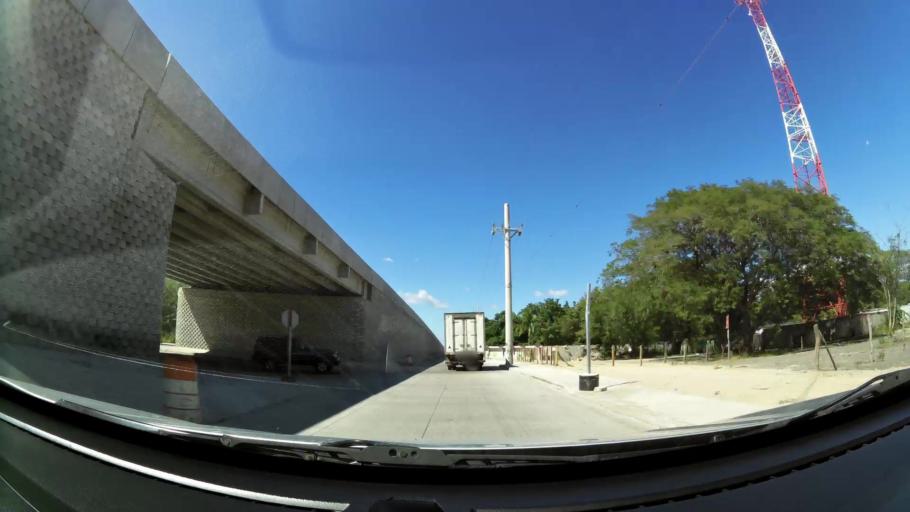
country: CR
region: Guanacaste
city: Liberia
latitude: 10.6119
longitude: -85.4339
